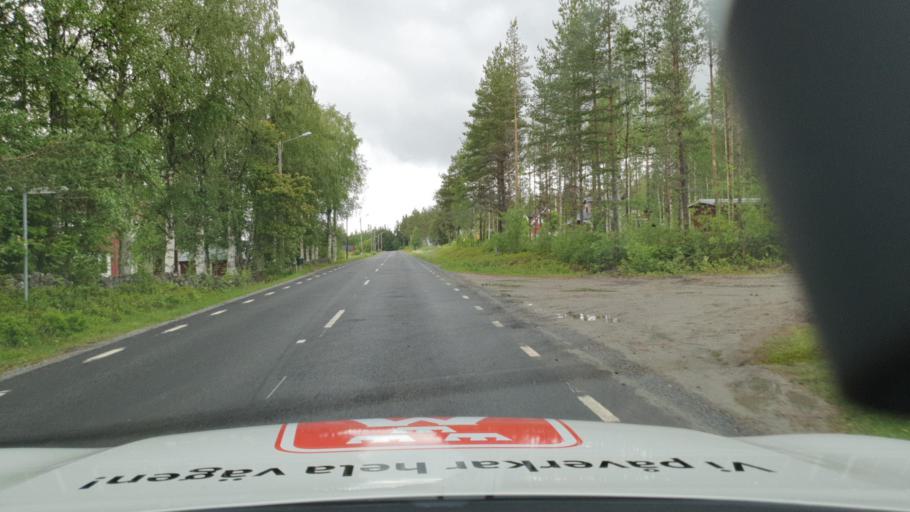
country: SE
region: Vaesterbotten
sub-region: Dorotea Kommun
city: Dorotea
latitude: 64.2347
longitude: 16.5419
